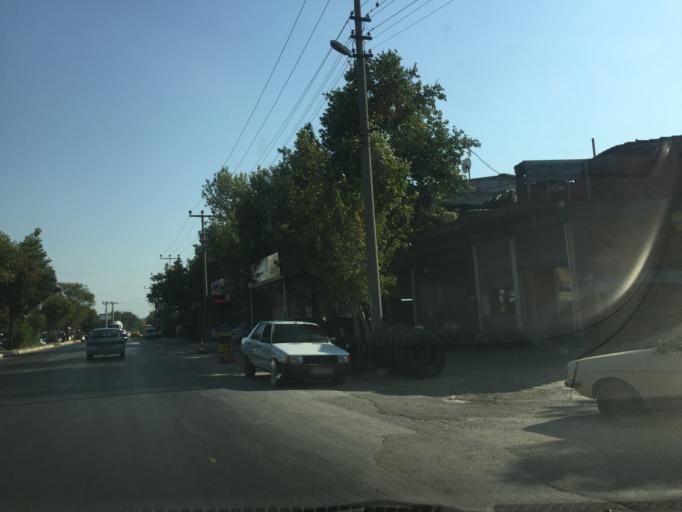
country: TR
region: Manisa
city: Akhisar
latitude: 38.9091
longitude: 27.8370
